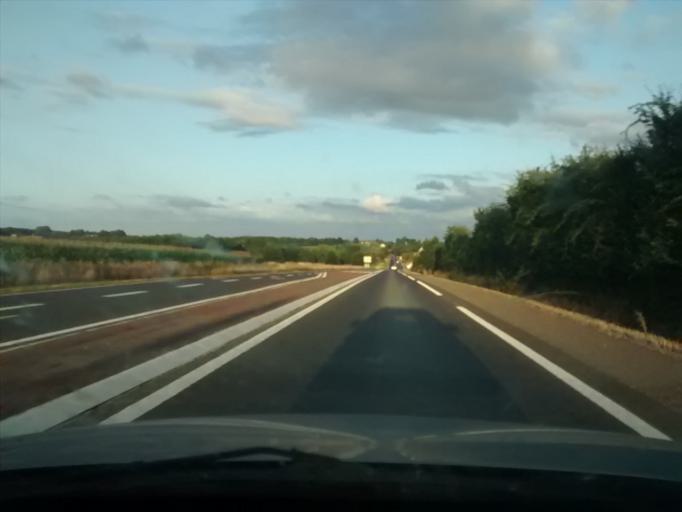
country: FR
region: Pays de la Loire
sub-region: Departement de la Sarthe
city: La Milesse
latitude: 48.0714
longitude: 0.1380
